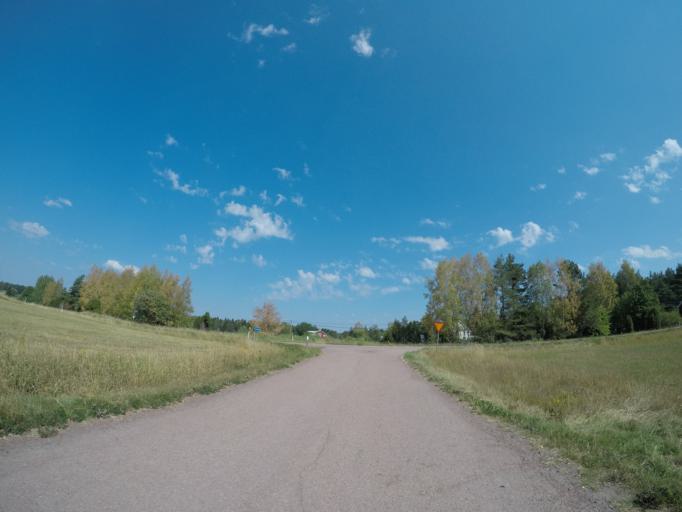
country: AX
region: Alands landsbygd
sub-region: Finstroem
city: Finstroem
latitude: 60.2105
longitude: 19.9045
